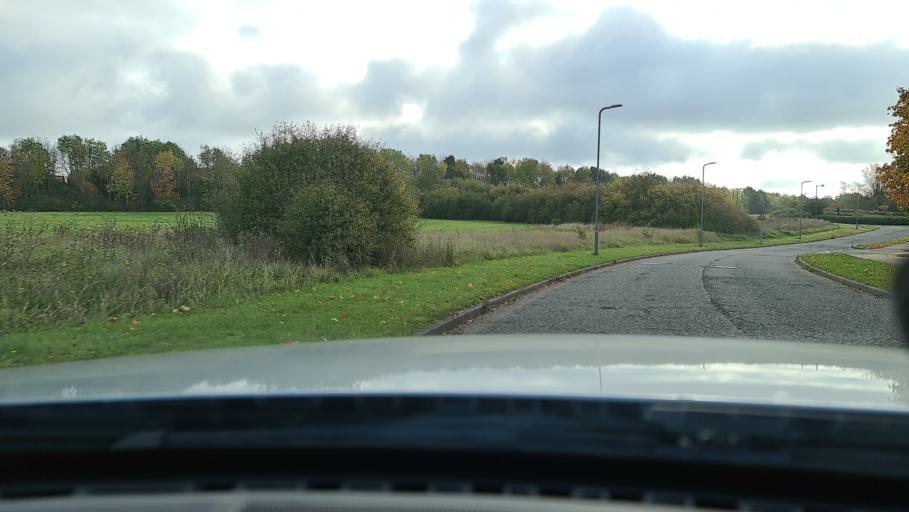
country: GB
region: England
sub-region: Milton Keynes
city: Simpson
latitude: 52.0266
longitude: -0.7014
